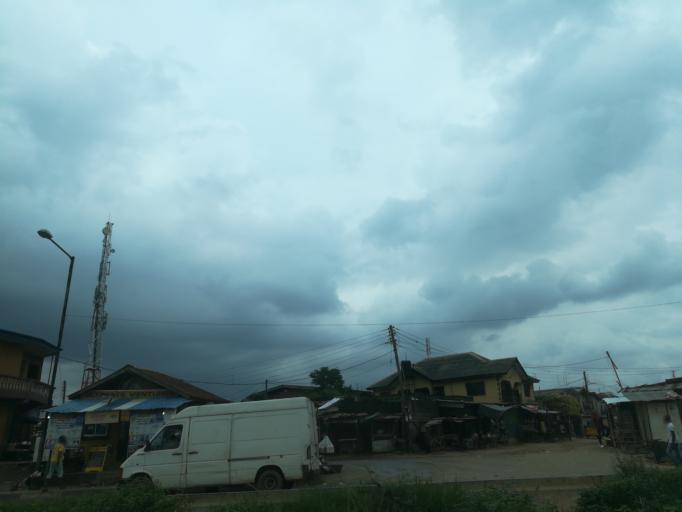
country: NG
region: Lagos
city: Ojota
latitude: 6.6196
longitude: 3.3963
